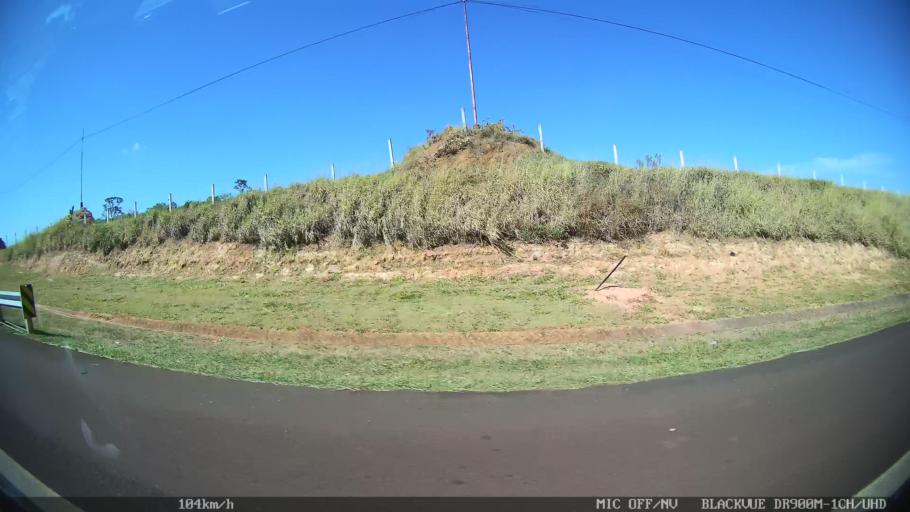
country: BR
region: Sao Paulo
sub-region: Franca
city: Franca
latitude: -20.5653
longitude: -47.4205
